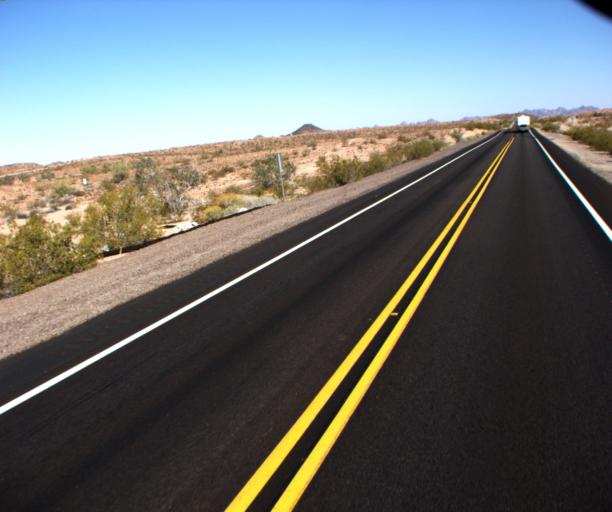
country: US
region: Arizona
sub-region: Yuma County
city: Wellton
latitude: 33.0842
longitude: -114.2962
